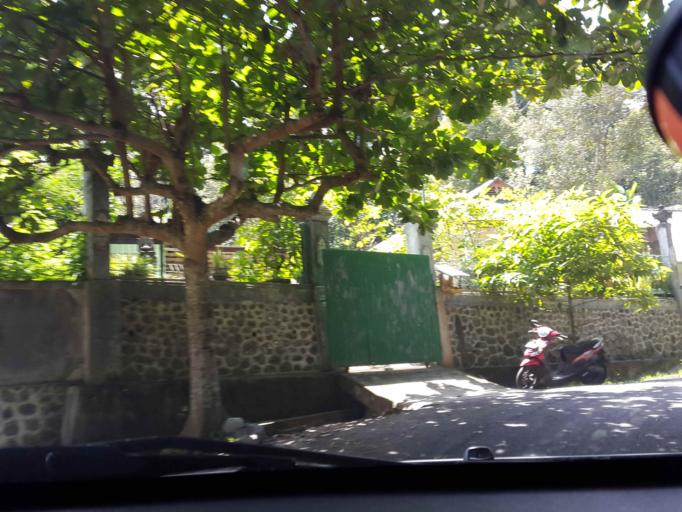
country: ID
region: Bali
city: Banjar Kelodan
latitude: -8.4987
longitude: 115.3947
